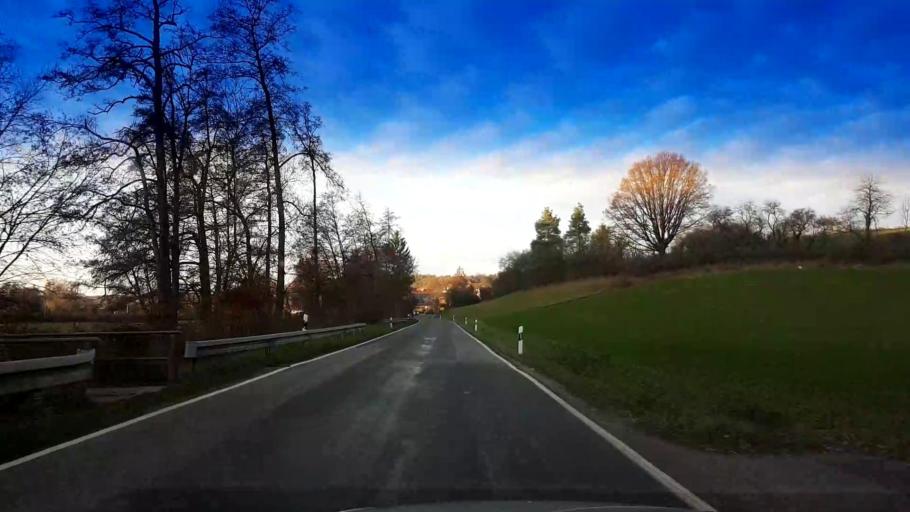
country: DE
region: Bavaria
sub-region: Upper Franconia
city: Walsdorf
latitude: 49.8786
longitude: 10.7629
